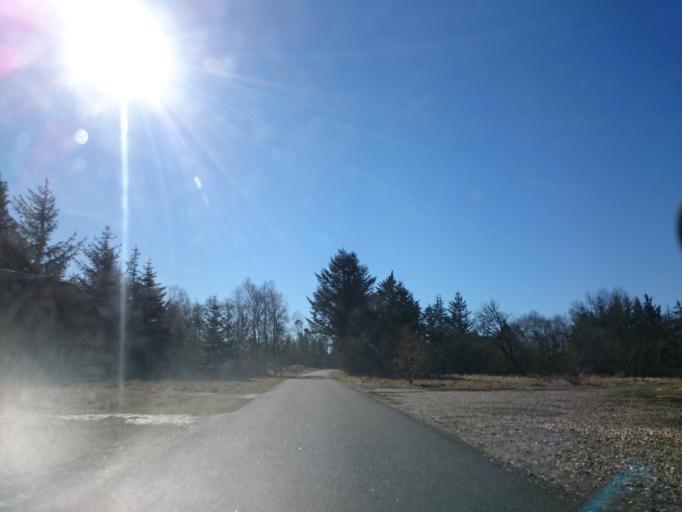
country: DK
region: North Denmark
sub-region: Hjorring Kommune
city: Sindal
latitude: 57.6223
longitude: 10.3159
